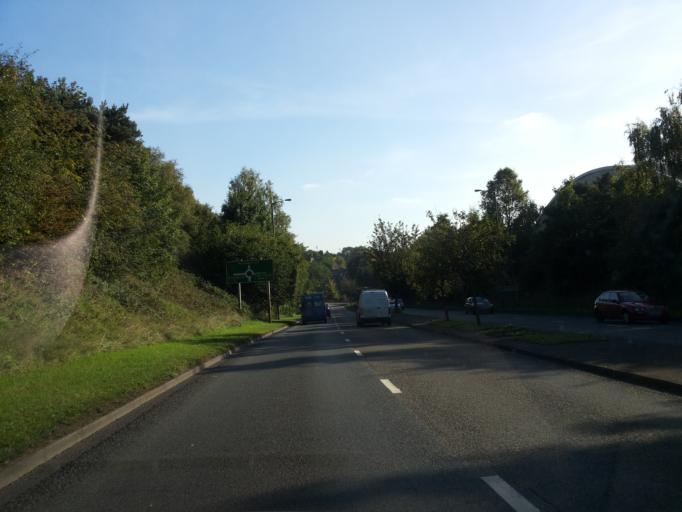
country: GB
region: England
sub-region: Worcestershire
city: Kidderminster
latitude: 52.3882
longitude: -2.2442
